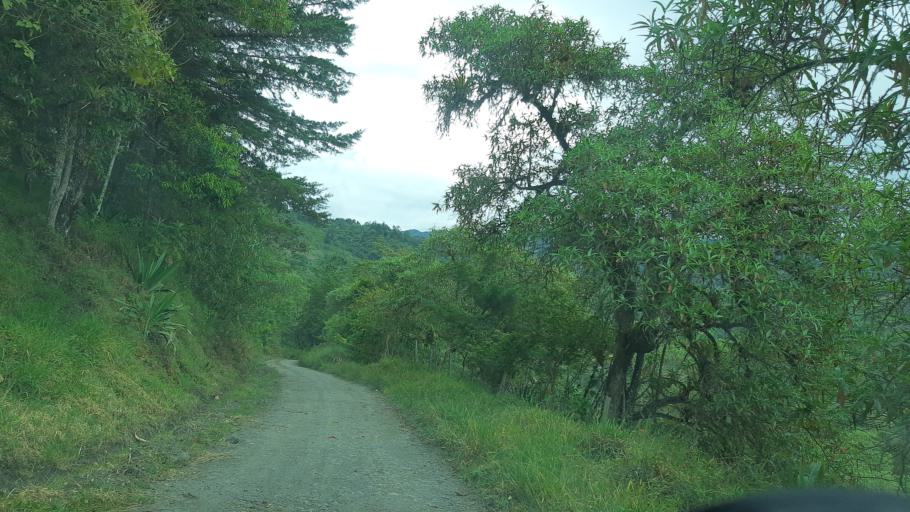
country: CO
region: Boyaca
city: Garagoa
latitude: 5.0415
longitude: -73.3385
